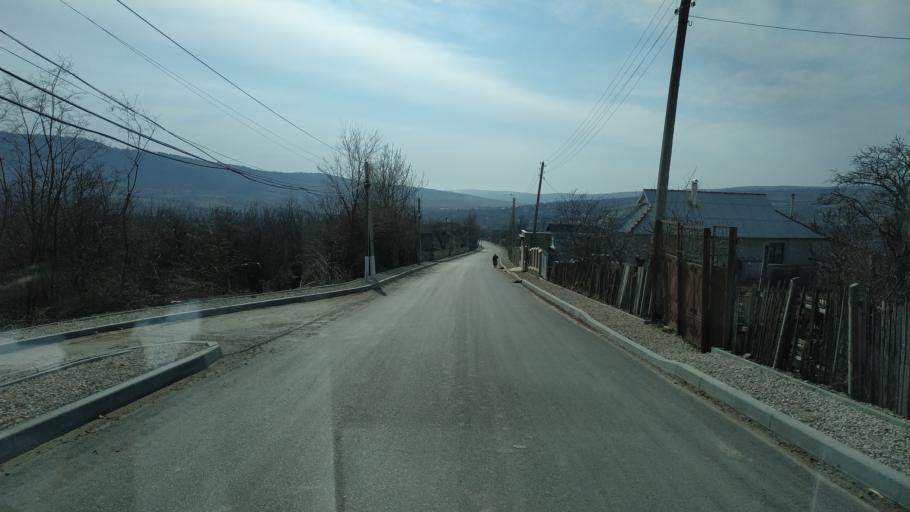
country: MD
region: Nisporeni
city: Nisporeni
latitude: 47.1698
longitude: 28.1308
